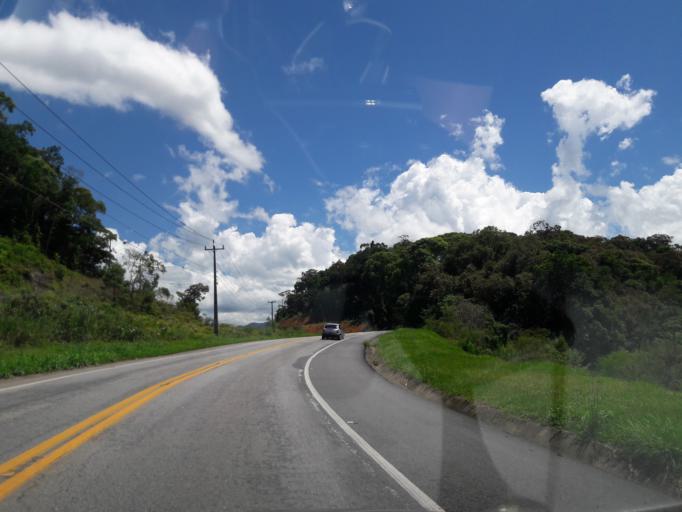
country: BR
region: Parana
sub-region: Antonina
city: Antonina
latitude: -25.4574
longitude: -48.8138
